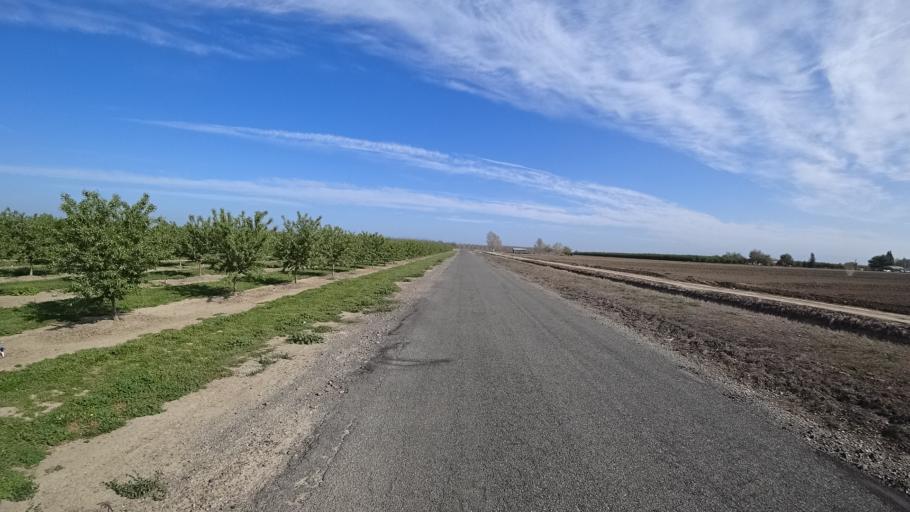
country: US
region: California
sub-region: Glenn County
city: Hamilton City
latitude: 39.6245
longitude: -122.0462
